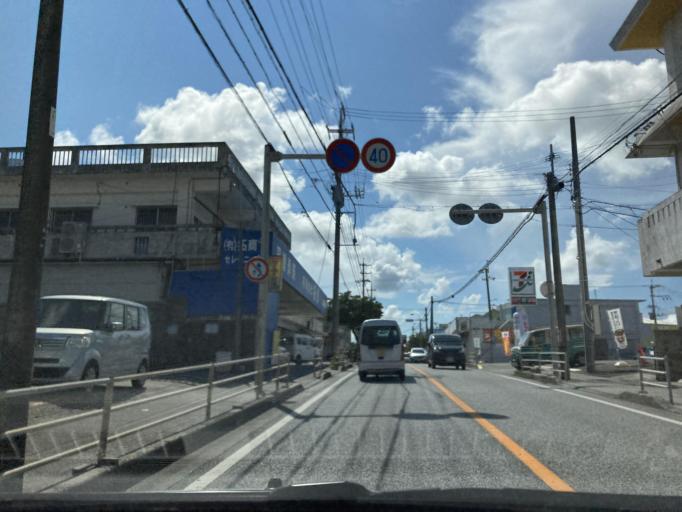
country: JP
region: Okinawa
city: Tomigusuku
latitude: 26.1863
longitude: 127.7110
